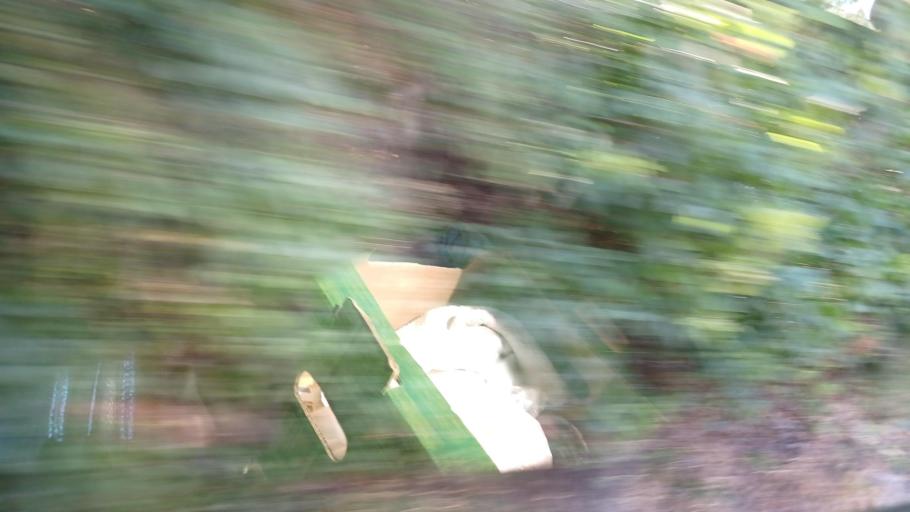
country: CY
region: Pafos
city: Mesogi
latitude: 34.9121
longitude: 32.6286
